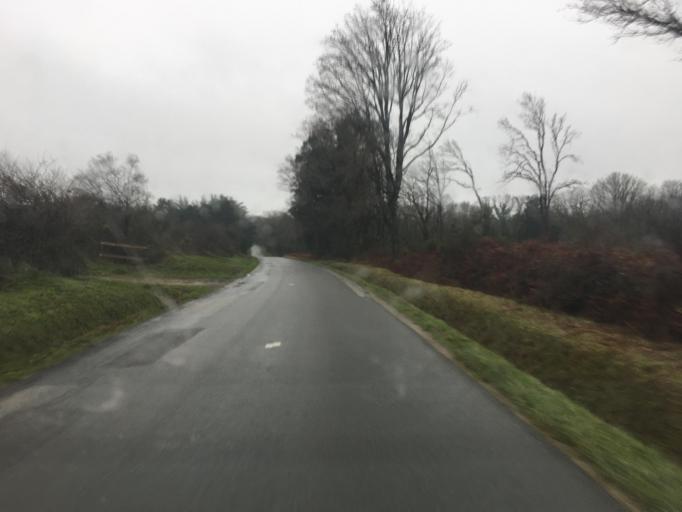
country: FR
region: Brittany
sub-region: Departement du Morbihan
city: Sarzeau
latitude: 47.5235
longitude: -2.6958
